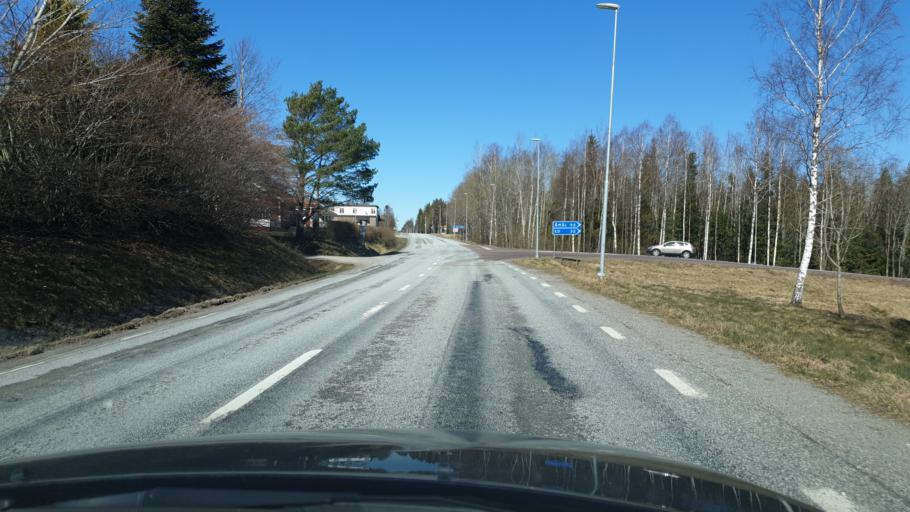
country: SE
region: Vaestra Goetaland
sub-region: Tanums Kommun
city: Tanumshede
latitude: 58.7963
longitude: 11.5620
